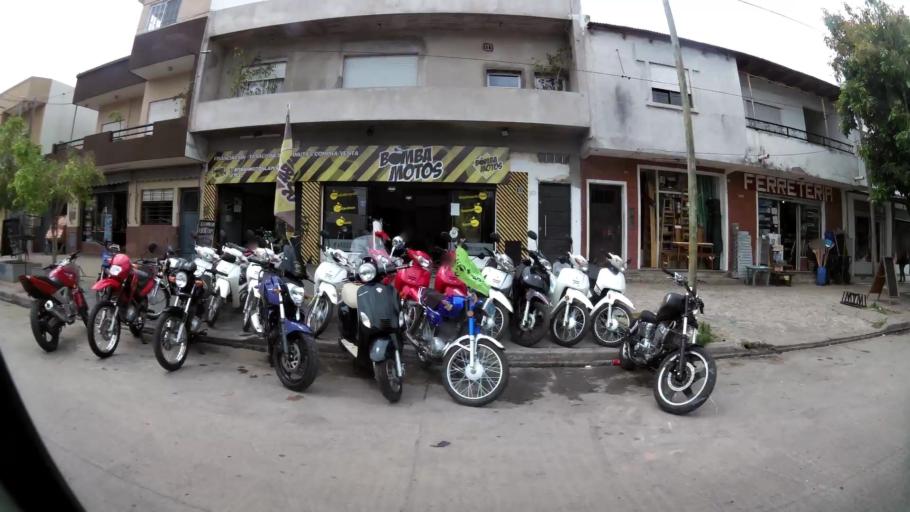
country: AR
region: Buenos Aires
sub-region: Partido de La Plata
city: La Plata
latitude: -34.9128
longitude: -57.9946
